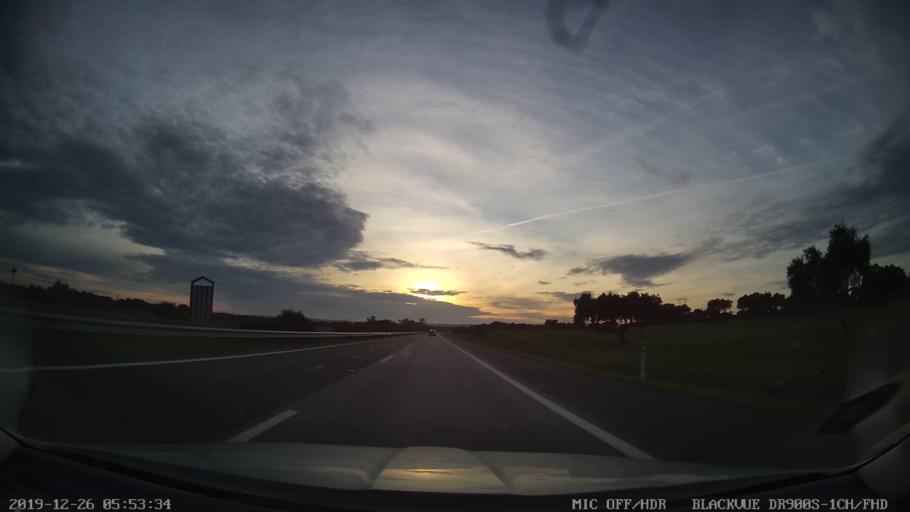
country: PT
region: Evora
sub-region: Evora
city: Evora
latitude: 38.6352
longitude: -7.8821
